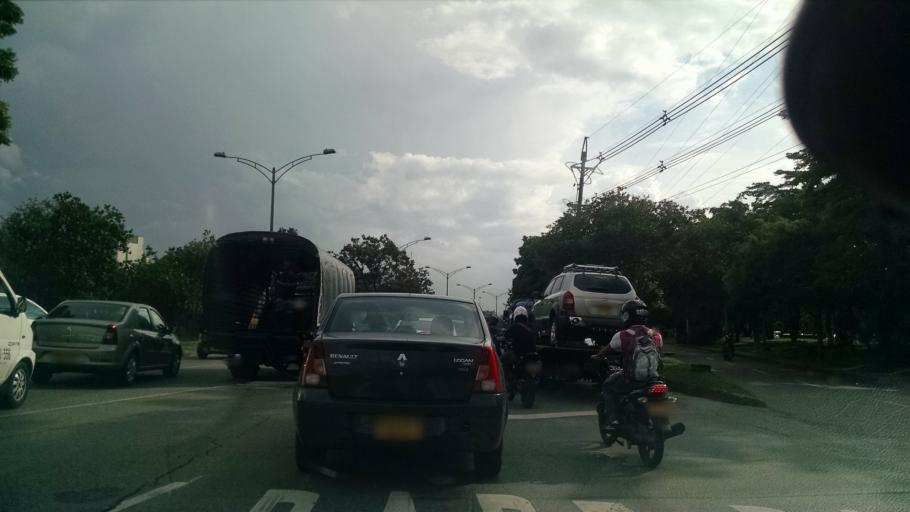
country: CO
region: Antioquia
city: Medellin
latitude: 6.2590
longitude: -75.5753
